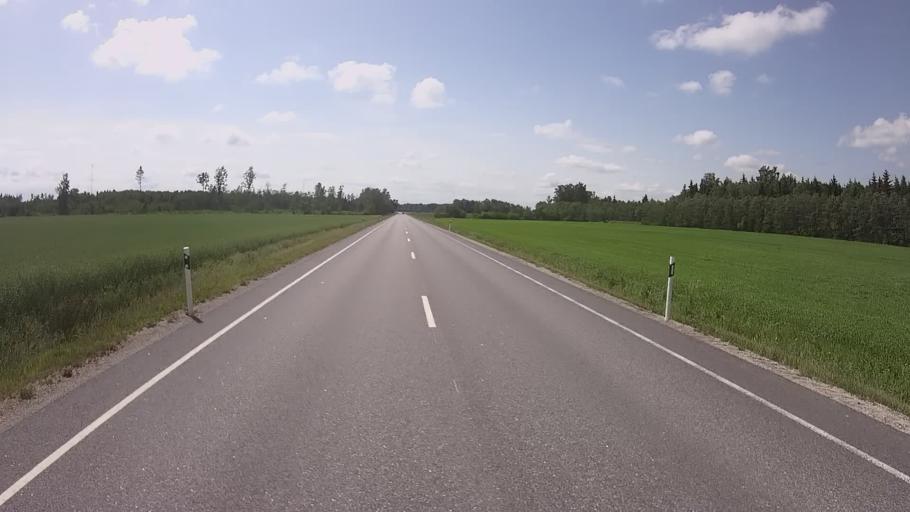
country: EE
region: Tartu
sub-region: Tartu linn
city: Tartu
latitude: 58.3867
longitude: 26.8892
